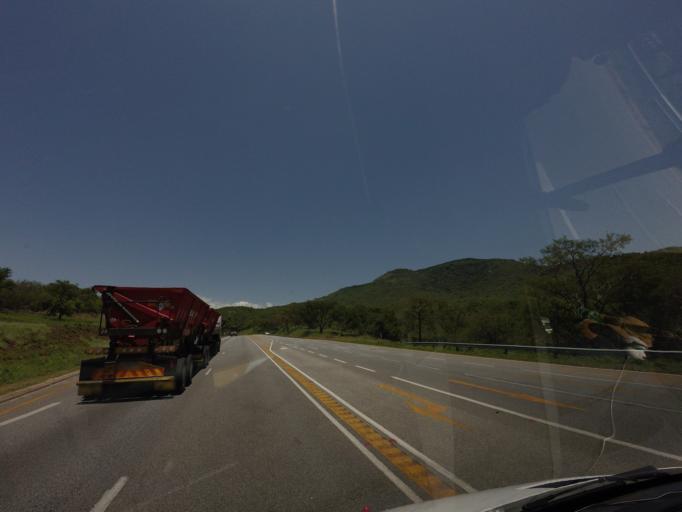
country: ZA
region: Mpumalanga
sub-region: Ehlanzeni District
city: Nelspruit
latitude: -25.4329
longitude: 30.7385
